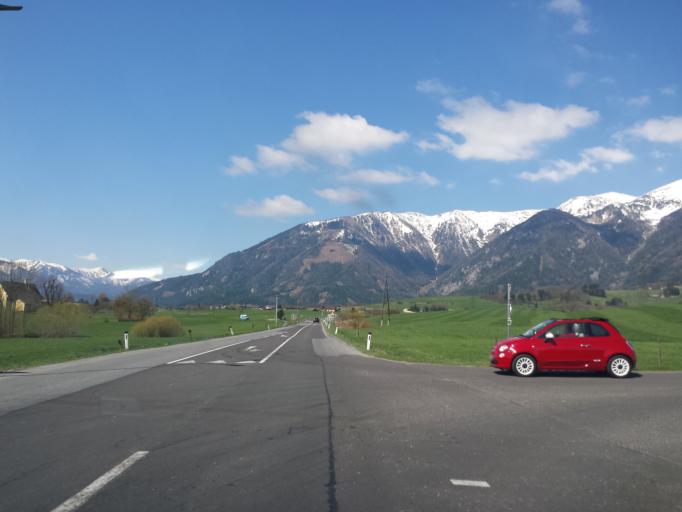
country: AT
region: Styria
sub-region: Politischer Bezirk Leoben
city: Trofaiach
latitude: 47.4081
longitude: 14.9740
